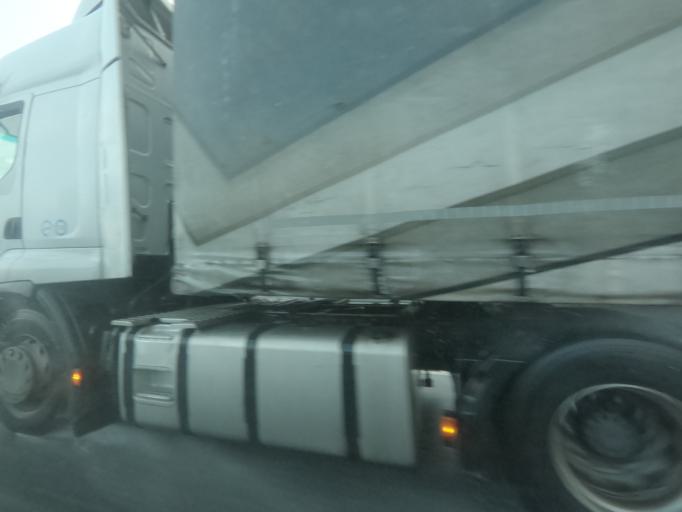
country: PT
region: Viana do Castelo
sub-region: Valenca
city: Valenza
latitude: 41.9929
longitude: -8.6439
